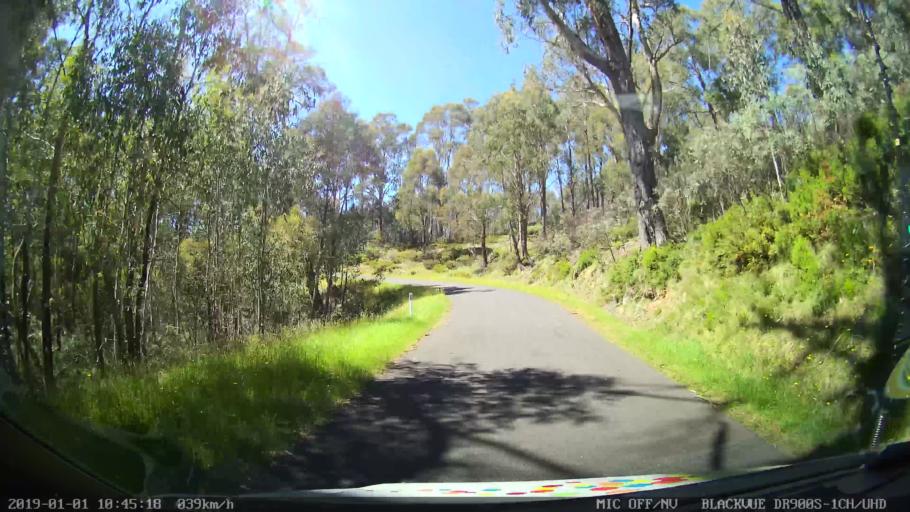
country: AU
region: New South Wales
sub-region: Snowy River
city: Jindabyne
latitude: -36.0352
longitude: 148.3369
